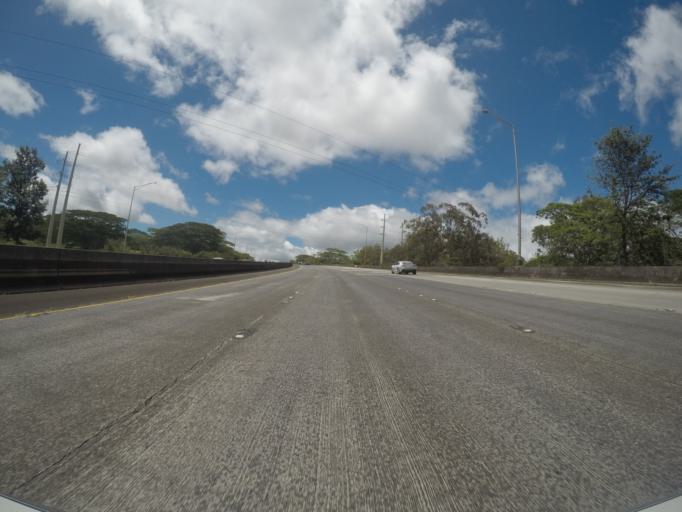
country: US
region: Hawaii
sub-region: Honolulu County
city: Mililani Town
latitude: 21.4458
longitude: -157.9915
